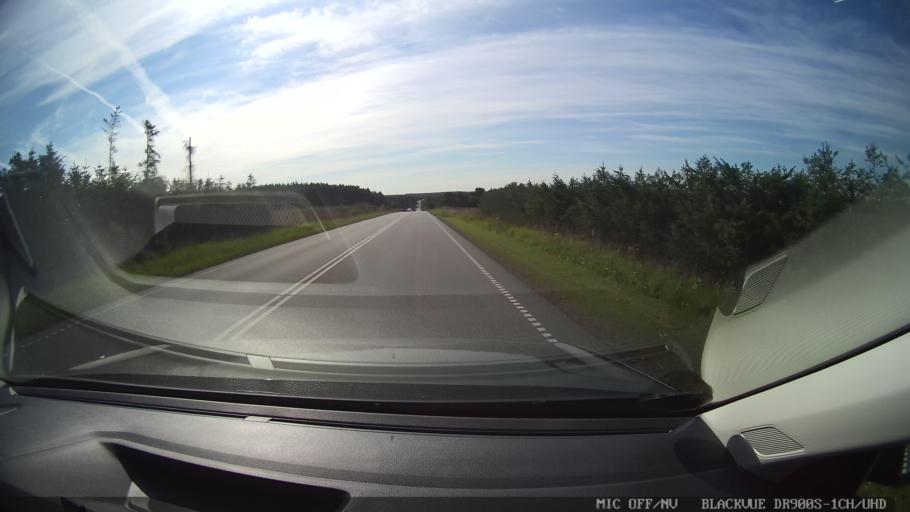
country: DK
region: North Denmark
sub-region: Mariagerfjord Kommune
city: Hadsund
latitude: 56.7633
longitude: 10.0656
